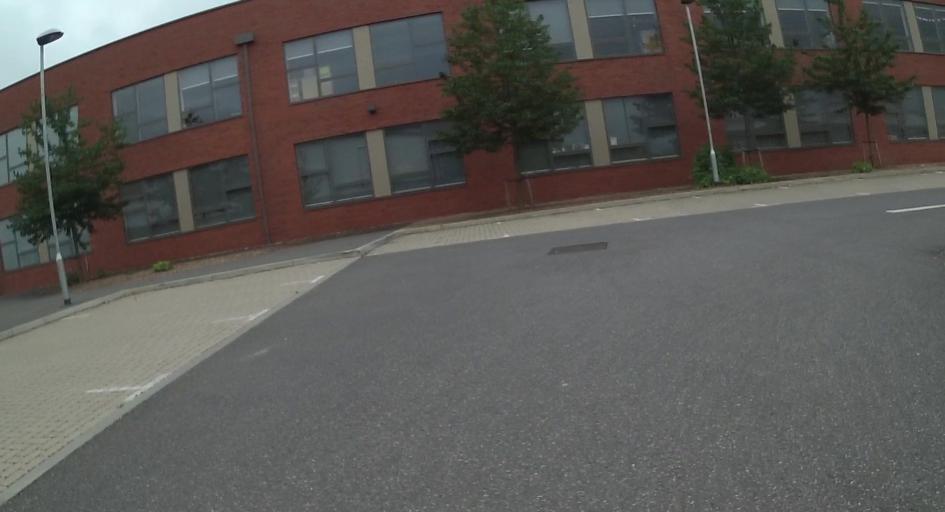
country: GB
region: England
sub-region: Hampshire
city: Eversley
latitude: 51.3793
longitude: -0.8941
